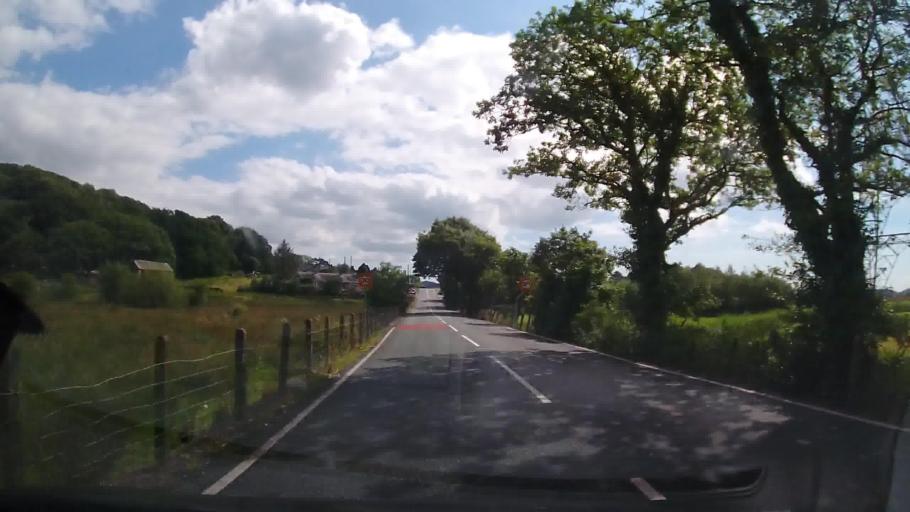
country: GB
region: Wales
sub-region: Gwynedd
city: Penrhyndeudraeth
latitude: 52.9201
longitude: -4.0499
